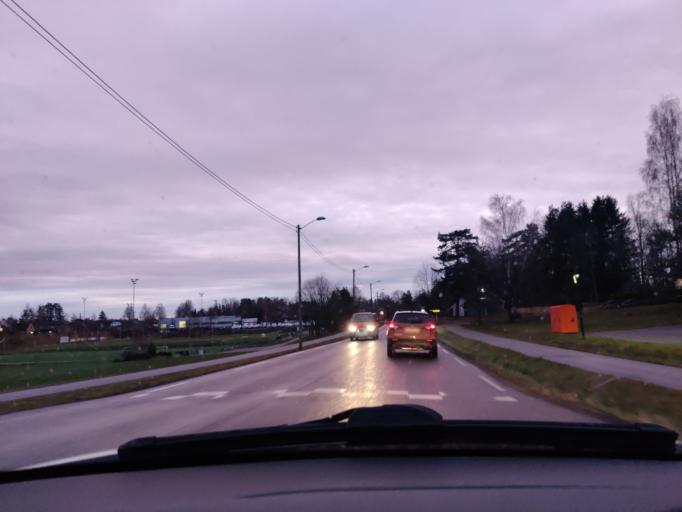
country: NO
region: Vestfold
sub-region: Tonsberg
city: Sem
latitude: 59.2568
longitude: 10.3594
